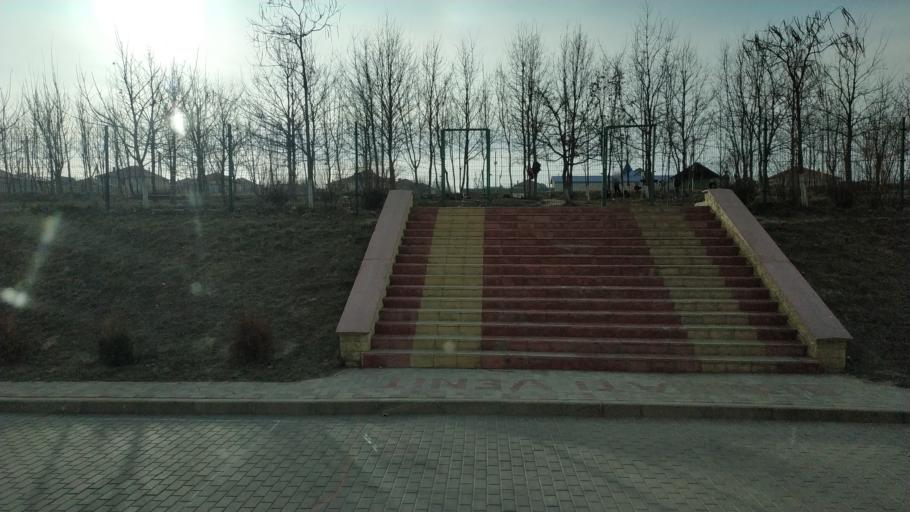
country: RO
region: Vaslui
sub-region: Comuna Dranceni
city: Dranceni
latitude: 46.8390
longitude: 28.1863
